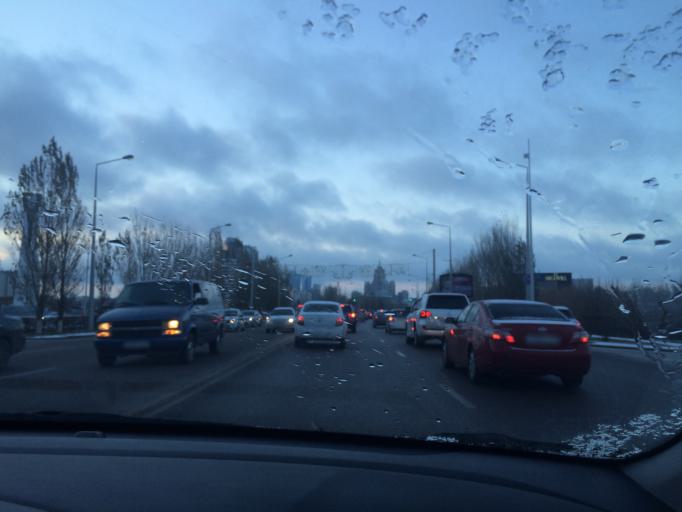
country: KZ
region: Astana Qalasy
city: Astana
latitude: 51.1549
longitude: 71.4121
